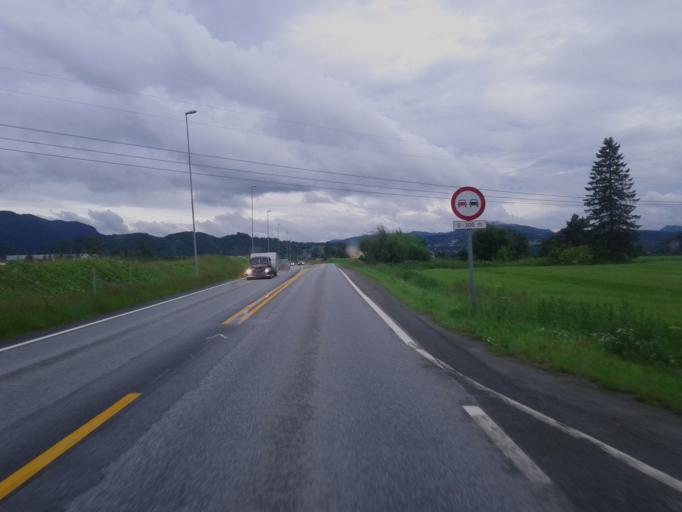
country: NO
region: Sor-Trondelag
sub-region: Melhus
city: Melhus
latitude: 63.3086
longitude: 10.2908
